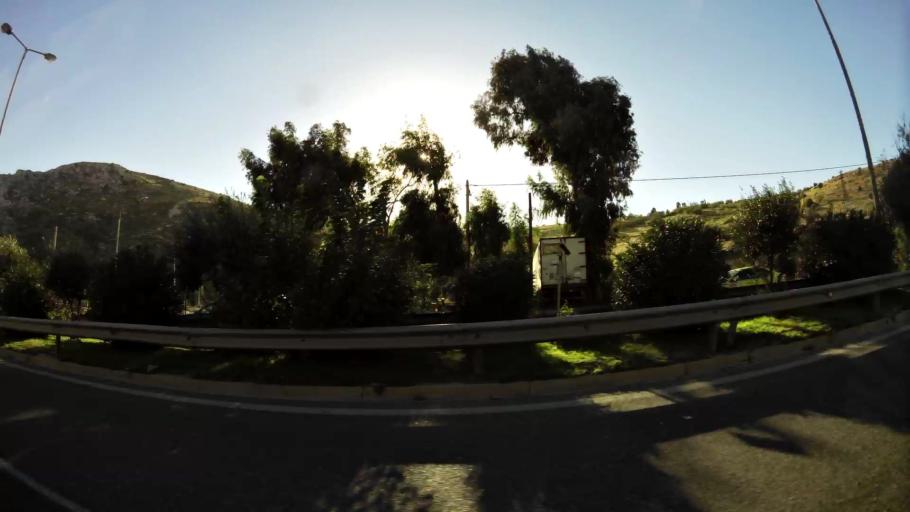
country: GR
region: Attica
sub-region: Nomos Piraios
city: Keratsini
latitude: 37.9734
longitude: 23.6000
